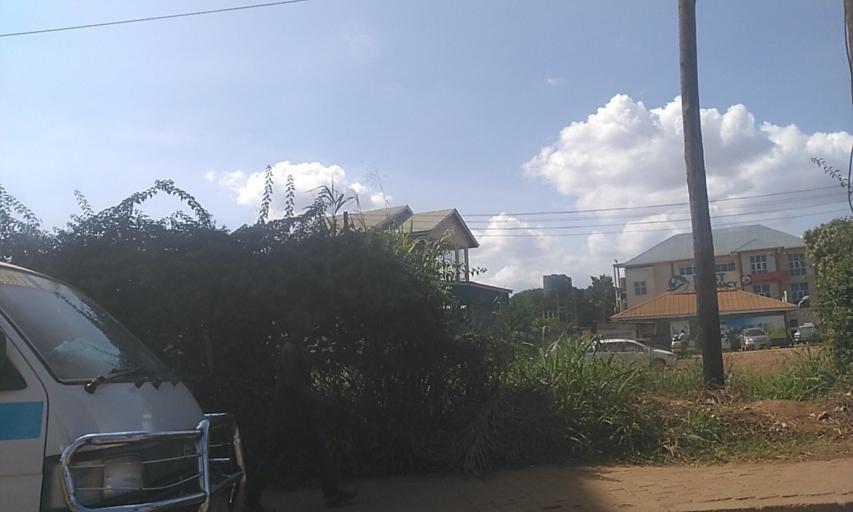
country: UG
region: Central Region
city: Kampala Central Division
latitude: 0.3348
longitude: 32.5773
